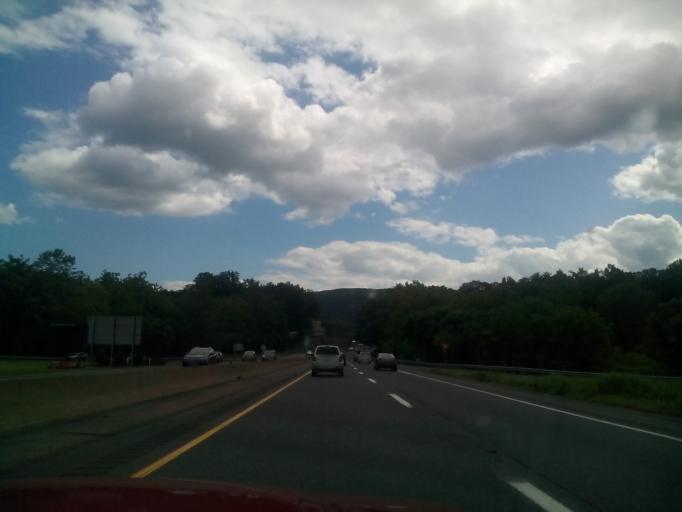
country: US
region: Pennsylvania
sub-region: Monroe County
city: East Stroudsburg
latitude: 40.9882
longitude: -75.1396
